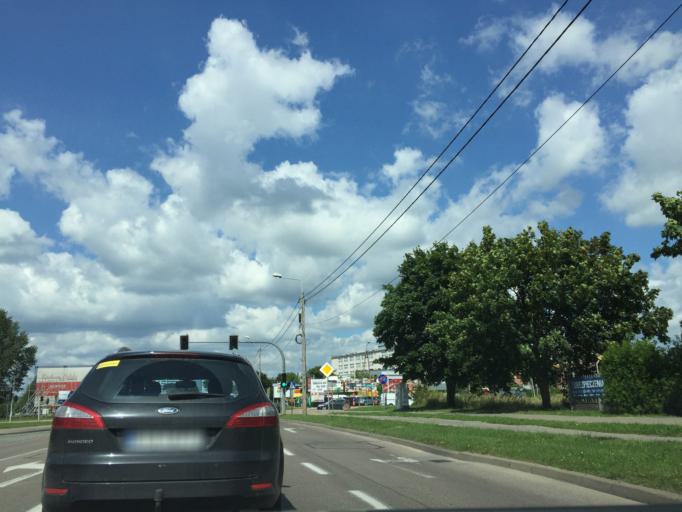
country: PL
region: Podlasie
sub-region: Bialystok
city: Bialystok
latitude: 53.1449
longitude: 23.1575
